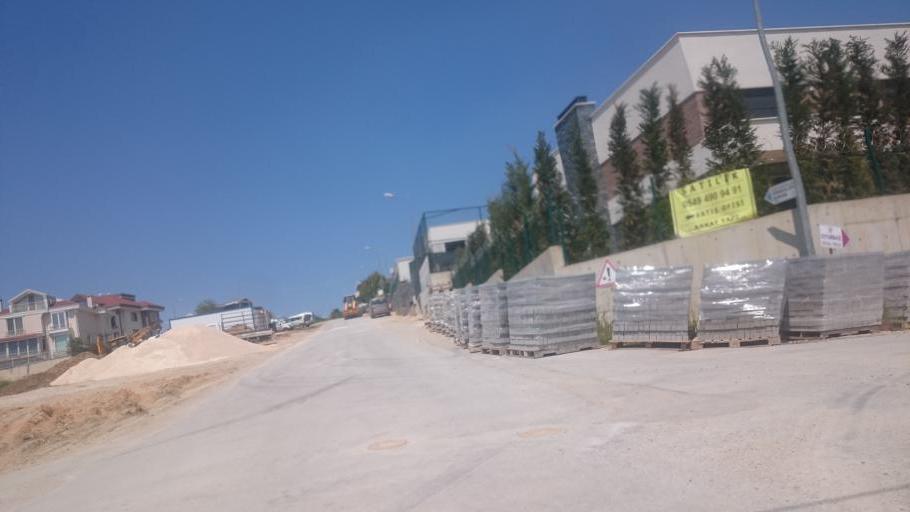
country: TR
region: Bursa
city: Gorukle
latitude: 40.2233
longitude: 28.8961
